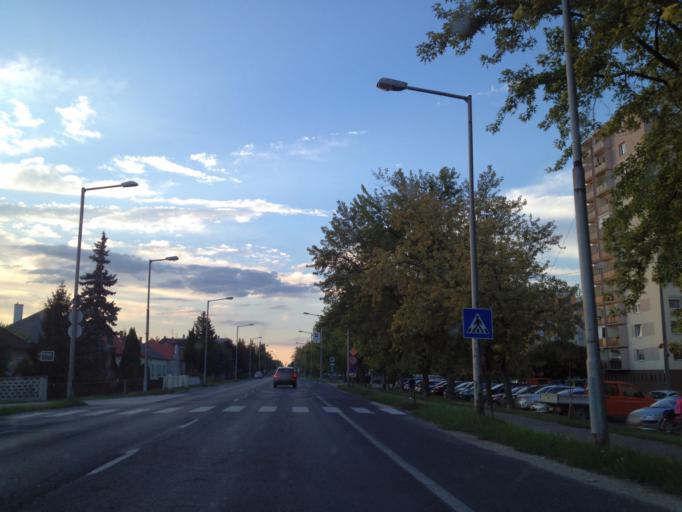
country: HU
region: Gyor-Moson-Sopron
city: Mosonmagyarovar
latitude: 47.8628
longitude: 17.2741
